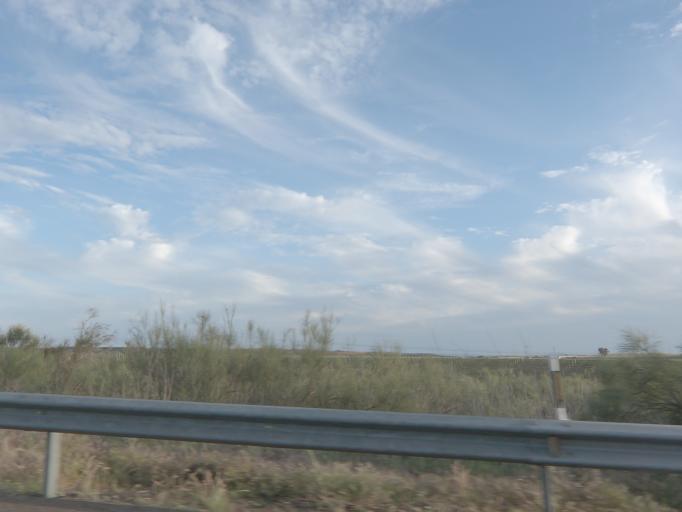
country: ES
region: Extremadura
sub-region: Provincia de Badajoz
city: Lobon
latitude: 38.8394
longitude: -6.6543
